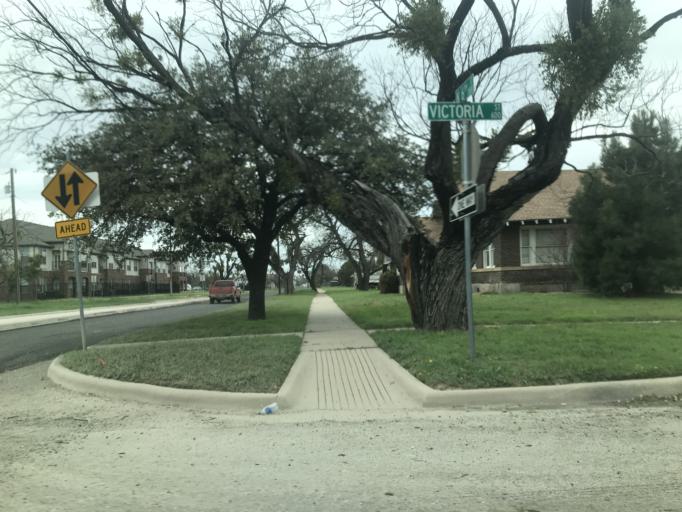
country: US
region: Texas
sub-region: Taylor County
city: Abilene
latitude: 32.4552
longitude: -99.7455
